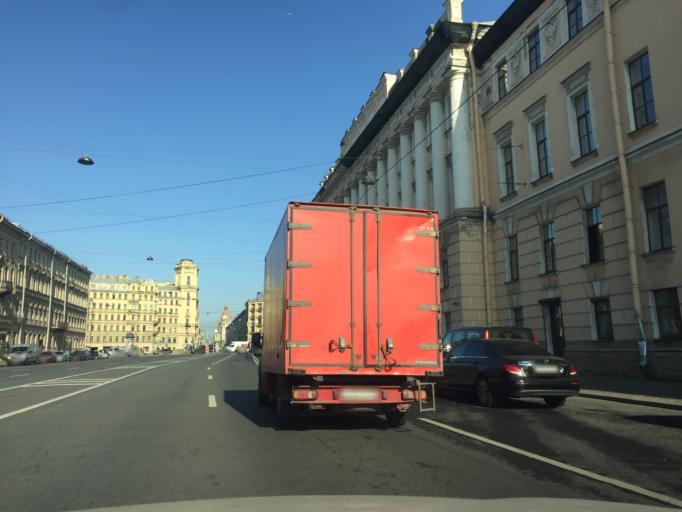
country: RU
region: St.-Petersburg
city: Saint Petersburg
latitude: 59.9176
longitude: 30.3077
